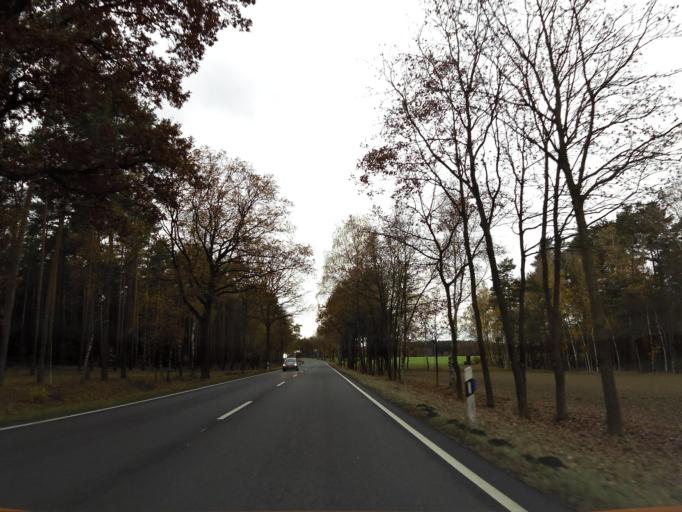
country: DE
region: Lower Saxony
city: Suhlendorf
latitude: 52.9289
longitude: 10.8306
